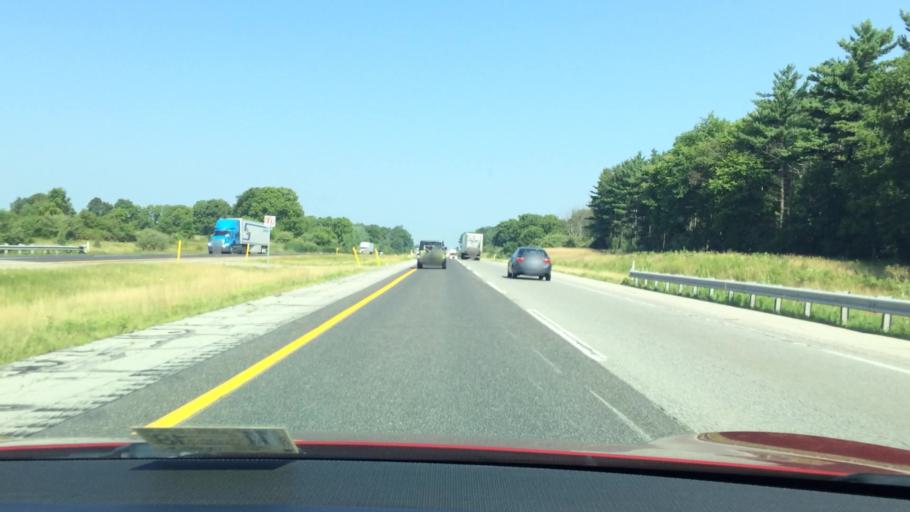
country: US
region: Indiana
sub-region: Steuben County
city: Fremont
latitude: 41.7052
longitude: -84.9268
